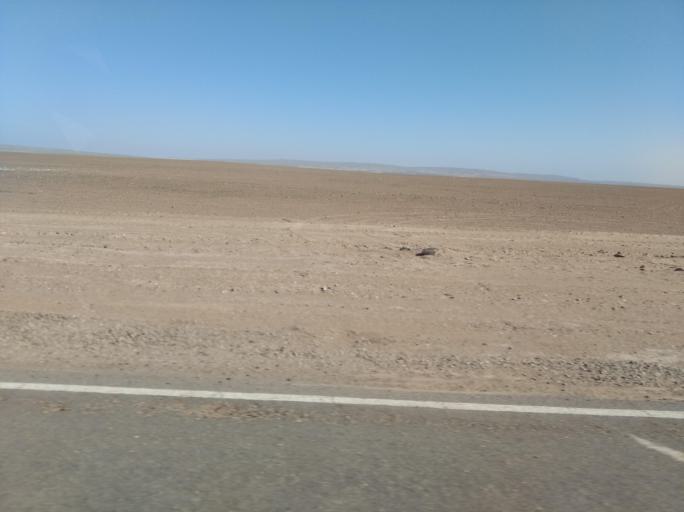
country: CL
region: Atacama
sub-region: Provincia de Copiapo
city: Copiapo
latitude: -27.3165
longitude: -70.8548
